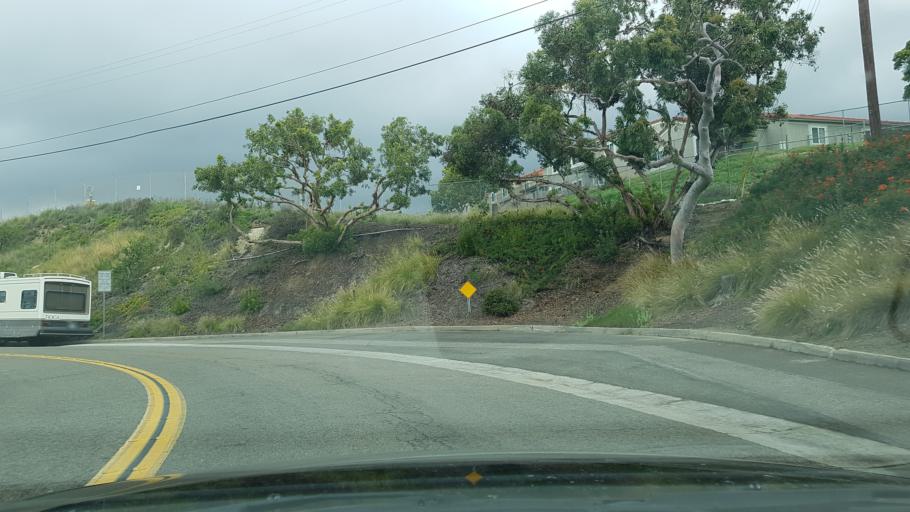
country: US
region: California
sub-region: San Diego County
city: Camp Pendleton South
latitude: 33.2126
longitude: -117.3941
